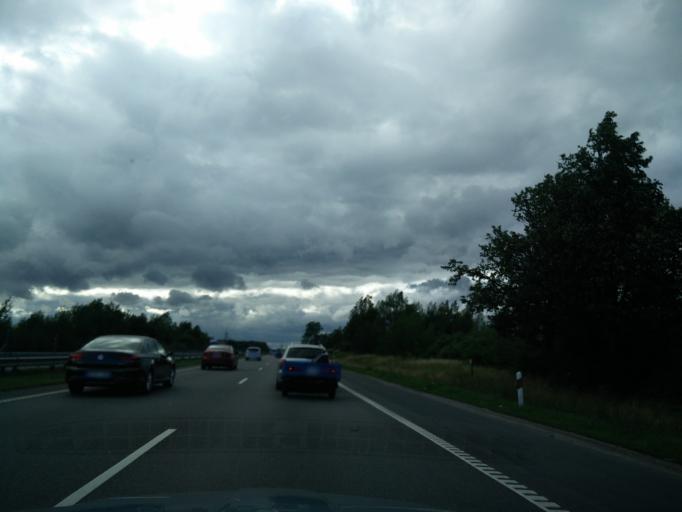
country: LT
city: Grigiskes
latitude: 54.6597
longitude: 25.1374
